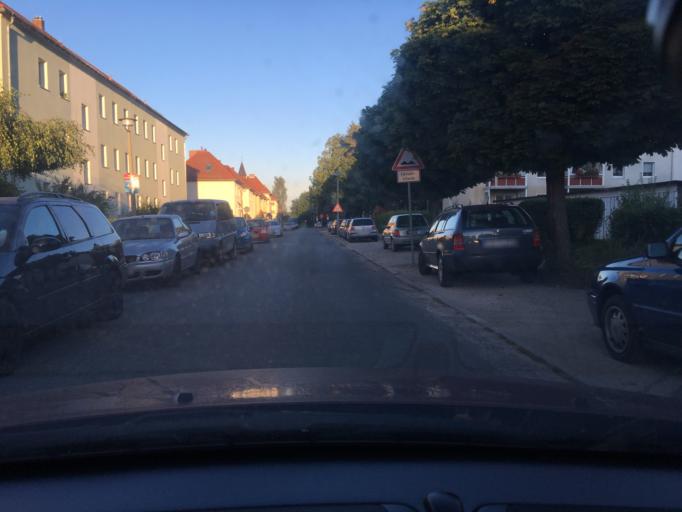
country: DE
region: Saxony
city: Goerlitz
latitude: 51.1435
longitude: 14.9469
